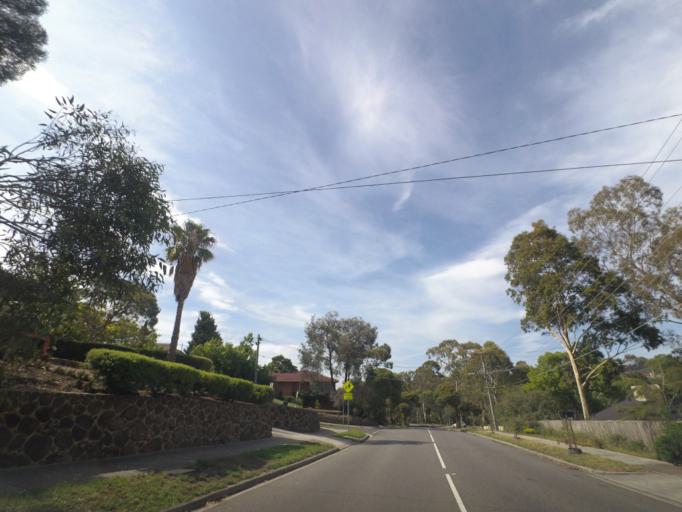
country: AU
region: Victoria
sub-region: Banyule
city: Viewbank
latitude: -37.7424
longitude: 145.0841
